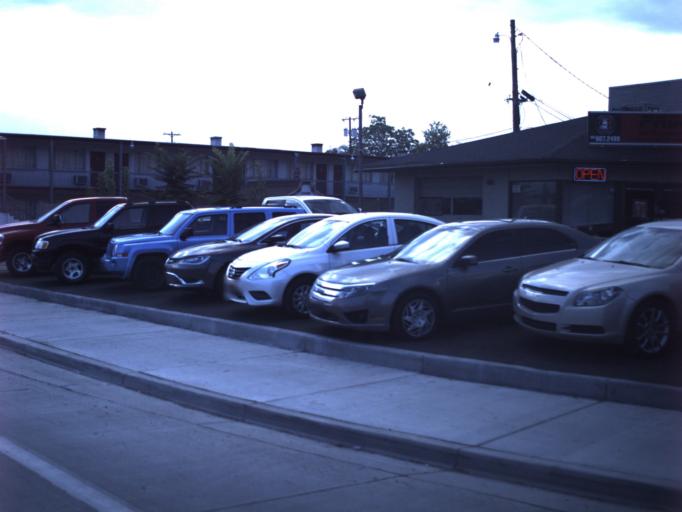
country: US
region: Utah
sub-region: Utah County
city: Provo
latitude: 40.2298
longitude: -111.6590
